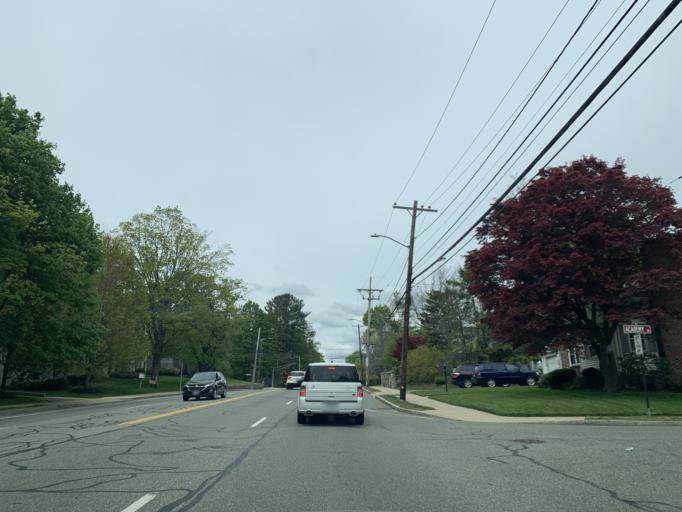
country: US
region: Massachusetts
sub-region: Norfolk County
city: Milton
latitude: 42.2536
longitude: -71.0765
